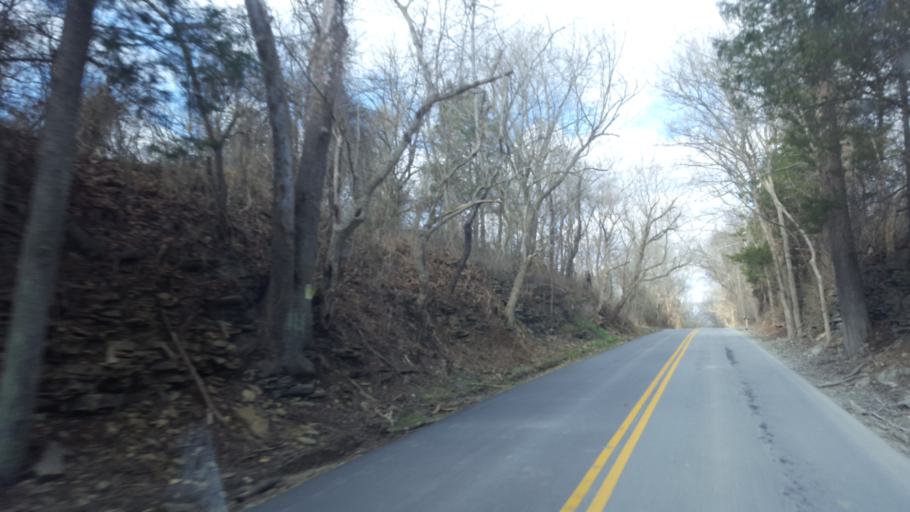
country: US
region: Kentucky
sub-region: Owen County
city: Owenton
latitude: 38.4583
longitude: -84.9588
